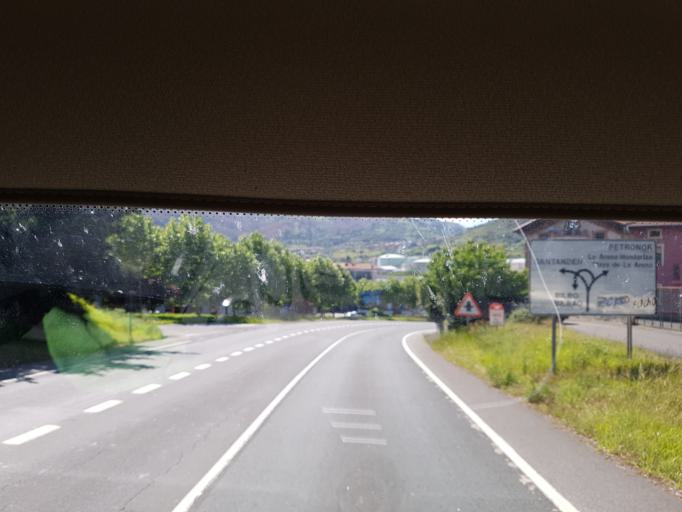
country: ES
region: Basque Country
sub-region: Bizkaia
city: San Julian de Muskiz
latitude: 43.3228
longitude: -3.1087
